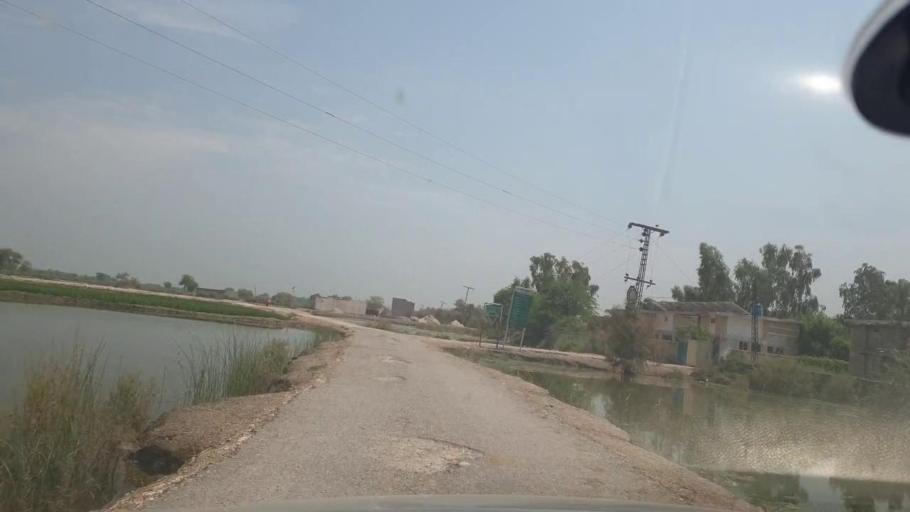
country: PK
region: Sindh
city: Thul
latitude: 28.1713
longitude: 68.6364
